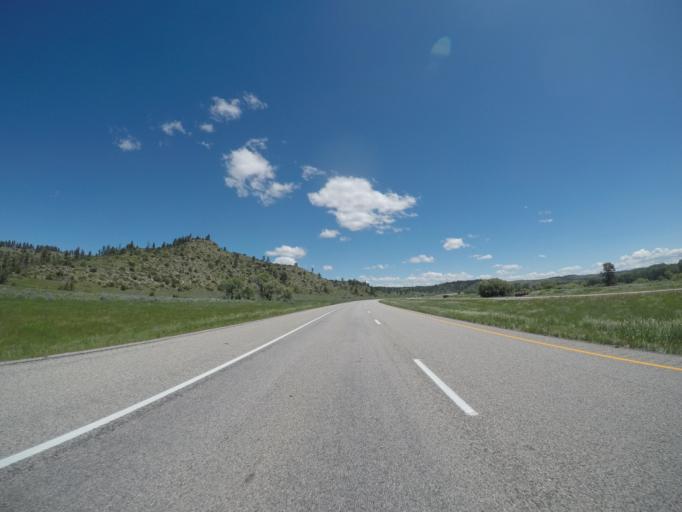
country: US
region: Montana
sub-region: Stillwater County
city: Columbus
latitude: 45.6963
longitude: -109.4091
